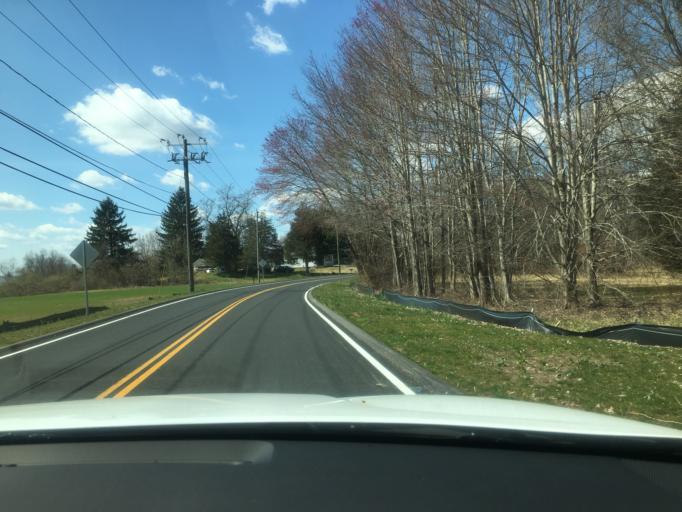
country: US
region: Connecticut
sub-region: Hartford County
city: Hazardville
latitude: 41.9588
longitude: -72.5280
